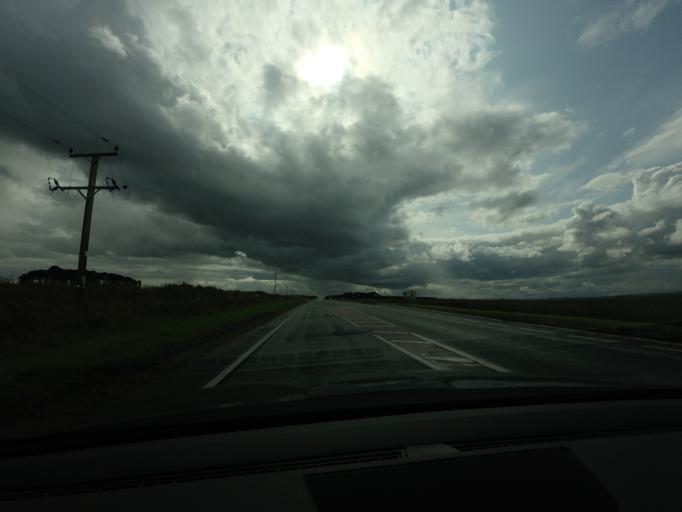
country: GB
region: Scotland
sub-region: Highland
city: Nairn
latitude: 57.5520
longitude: -3.9841
